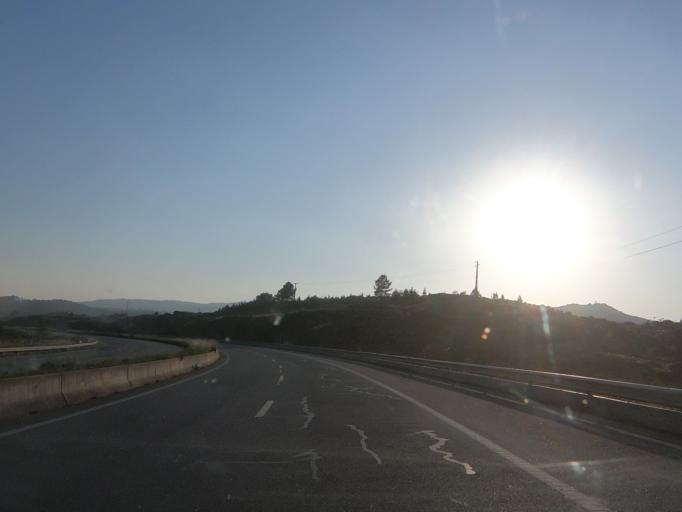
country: PT
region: Guarda
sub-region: Celorico da Beira
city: Celorico da Beira
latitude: 40.6359
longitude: -7.4558
